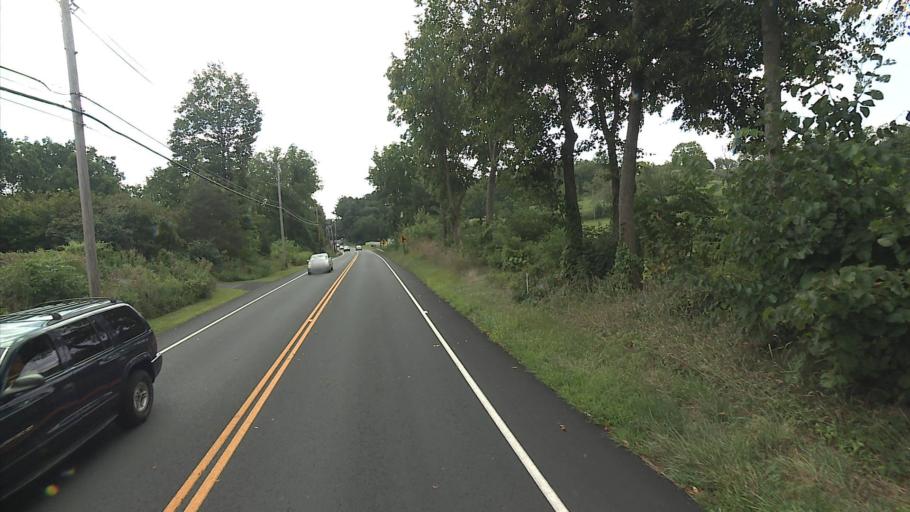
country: US
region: Connecticut
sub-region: Hartford County
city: West Hartford
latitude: 41.8174
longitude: -72.7665
